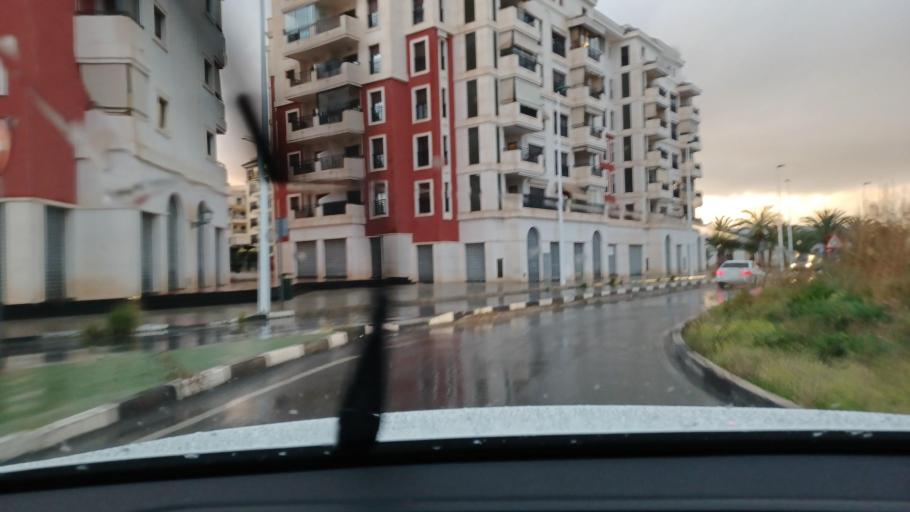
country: ES
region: Valencia
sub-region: Provincia de Alicante
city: Elche
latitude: 38.2532
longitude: -0.6974
